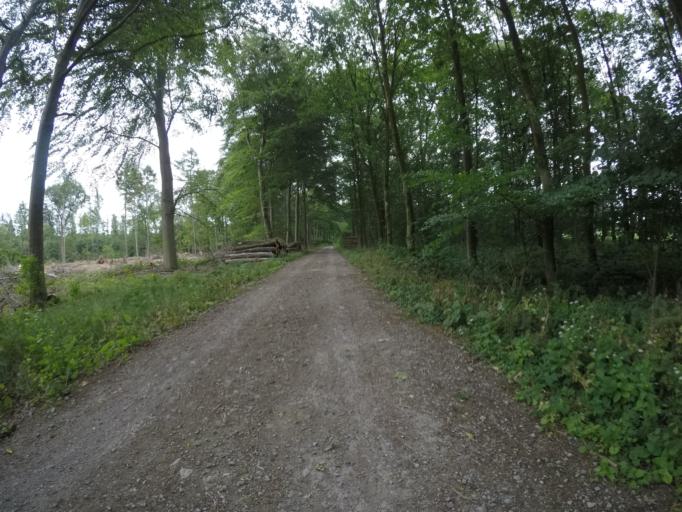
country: NL
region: Gelderland
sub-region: Oude IJsselstreek
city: Gendringen
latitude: 51.8671
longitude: 6.4114
